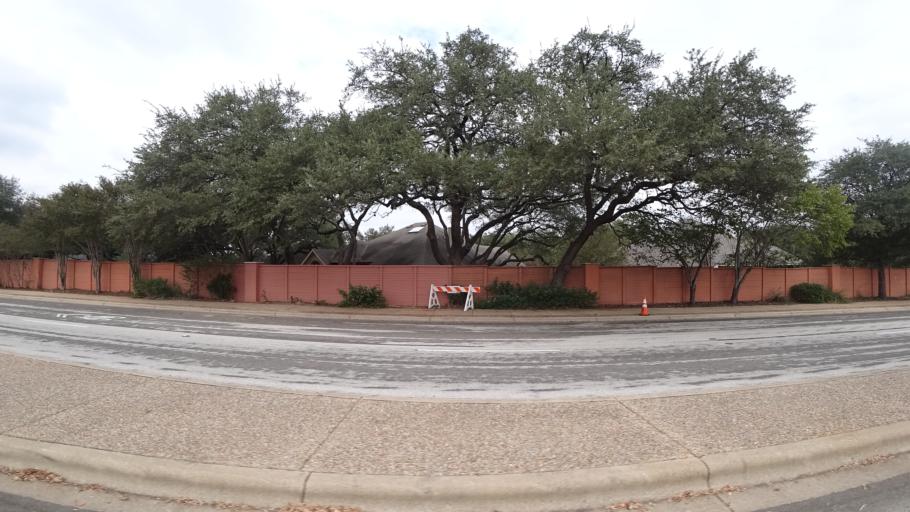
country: US
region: Texas
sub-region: Travis County
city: Shady Hollow
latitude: 30.2118
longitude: -97.8775
